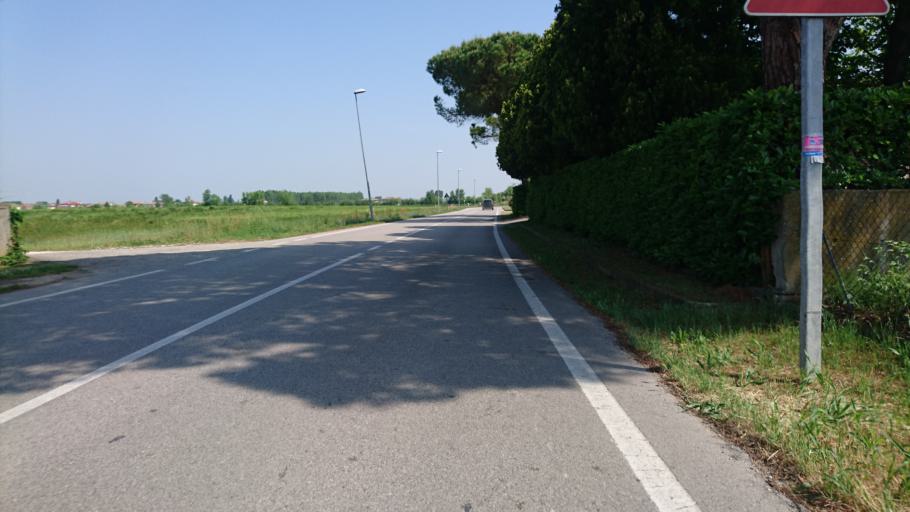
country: IT
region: Veneto
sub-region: Provincia di Venezia
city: Campagna Lupia
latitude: 45.3591
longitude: 12.1092
